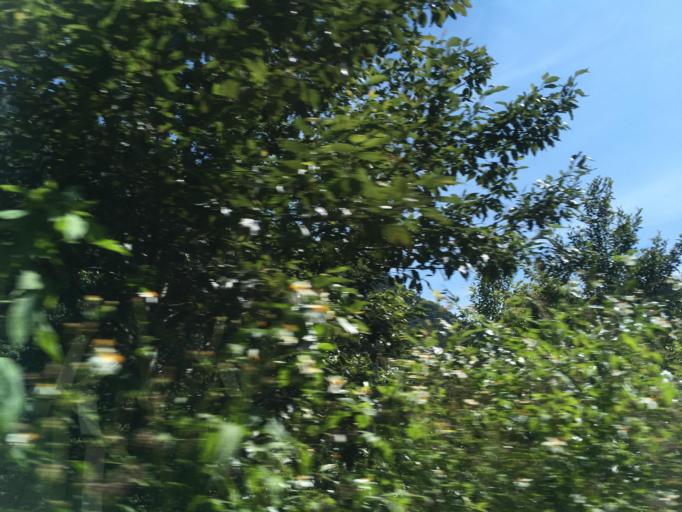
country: TW
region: Taiwan
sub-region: Yilan
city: Yilan
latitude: 24.4204
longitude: 121.7319
